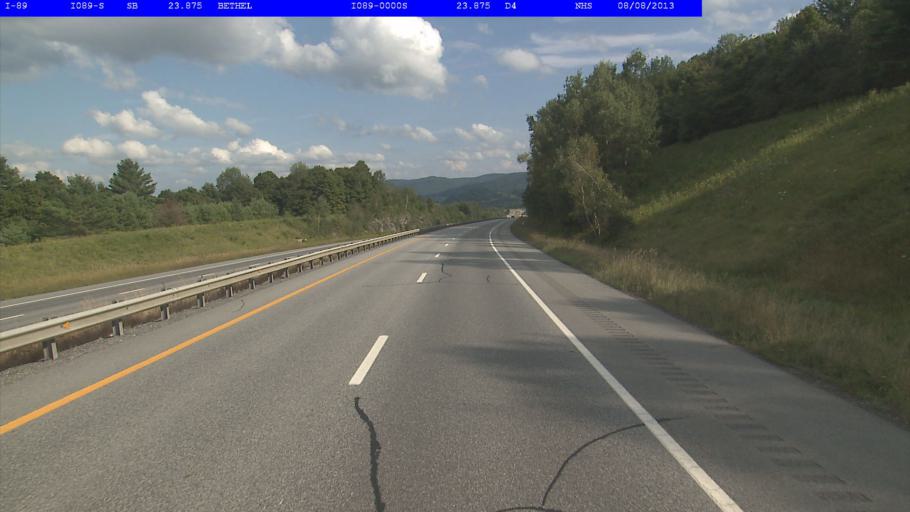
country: US
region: Vermont
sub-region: Orange County
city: Randolph
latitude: 43.8476
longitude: -72.5999
